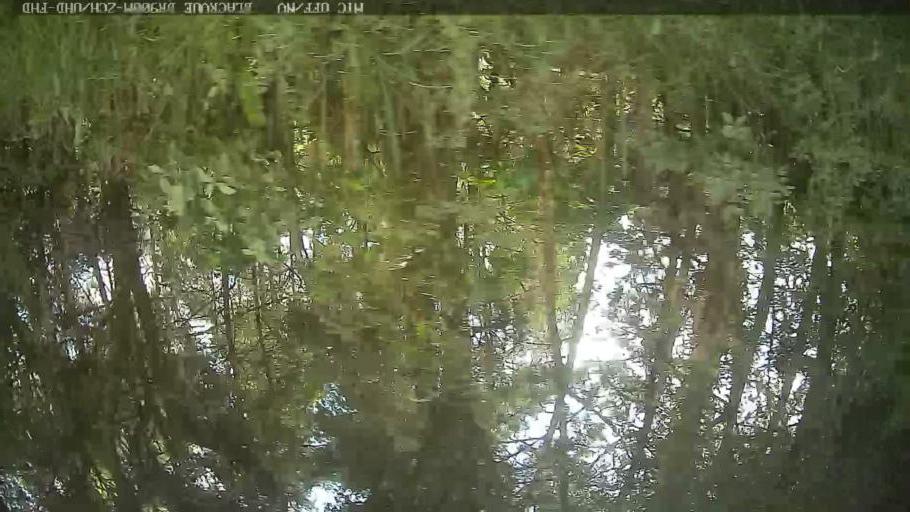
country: BR
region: Sao Paulo
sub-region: Atibaia
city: Atibaia
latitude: -23.0958
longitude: -46.5485
